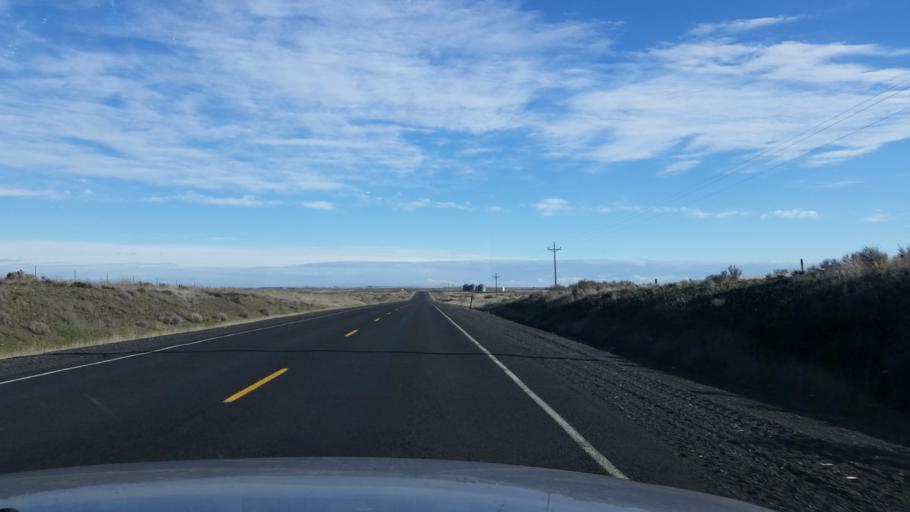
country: US
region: Washington
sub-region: Grant County
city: Warden
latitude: 47.3143
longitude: -118.7913
